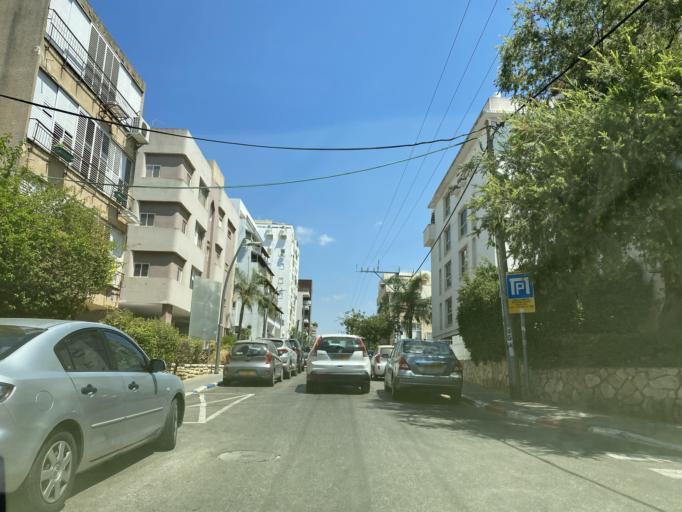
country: IL
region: Tel Aviv
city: Herzliyya
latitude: 32.1664
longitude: 34.8454
